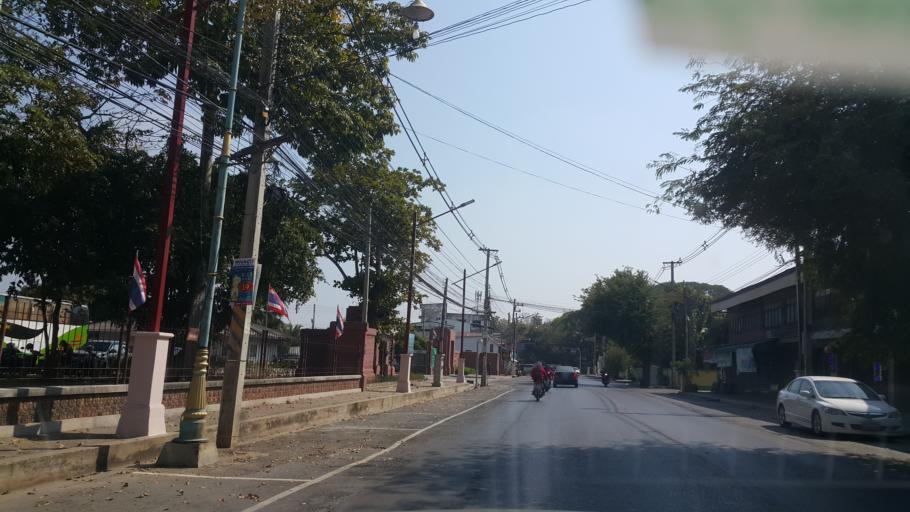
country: TH
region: Nakhon Ratchasima
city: Phimai
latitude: 15.2239
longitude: 102.4942
